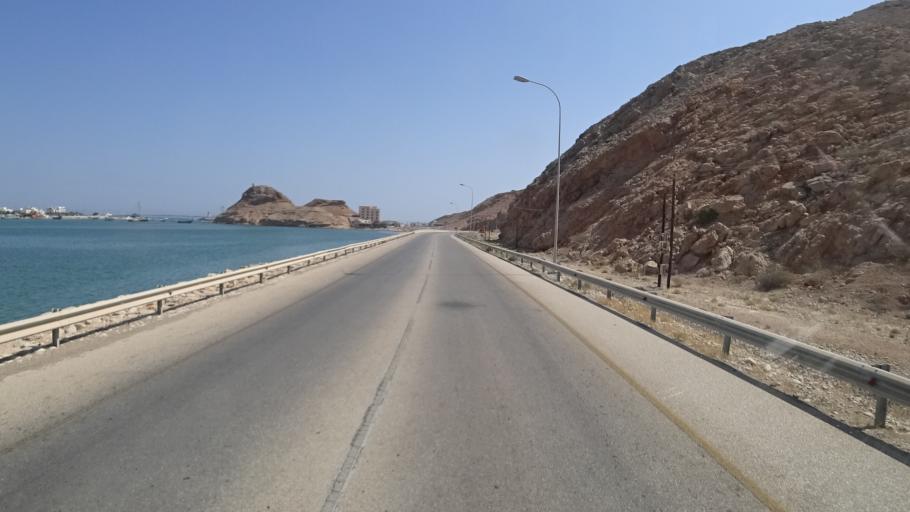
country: OM
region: Ash Sharqiyah
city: Sur
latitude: 22.5550
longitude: 59.5384
